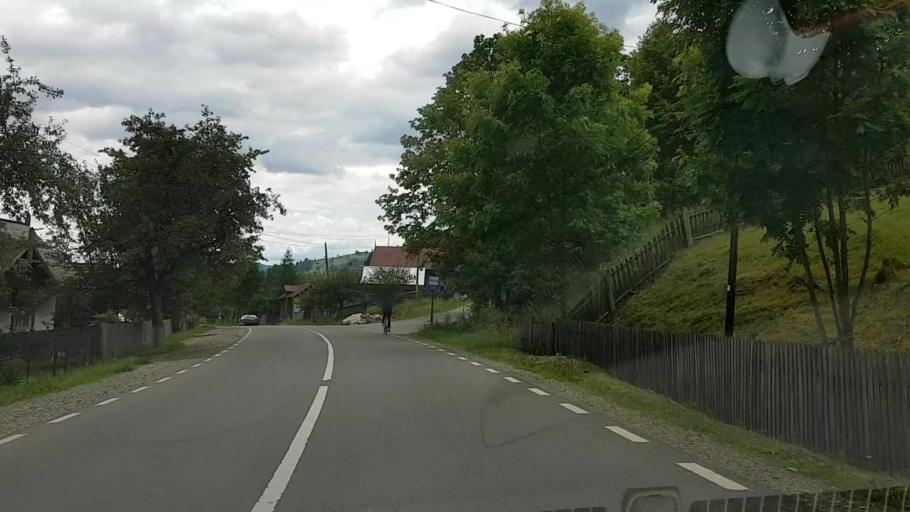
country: RO
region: Neamt
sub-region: Comuna Borca
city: Borca
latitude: 47.1850
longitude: 25.7747
